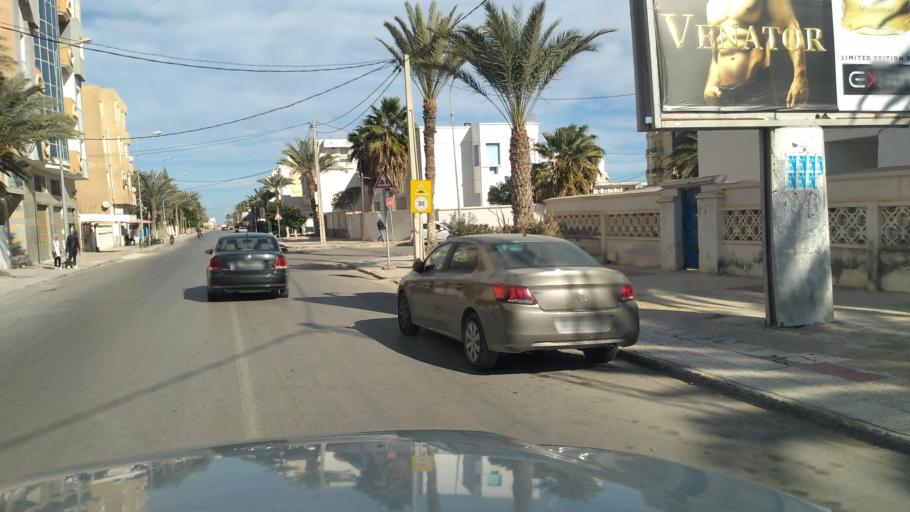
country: TN
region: Qabis
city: Gabes
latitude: 33.8890
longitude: 10.1114
